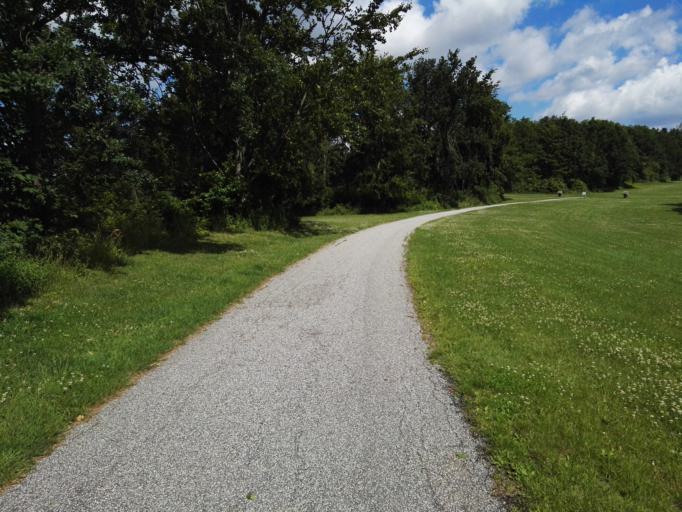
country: DK
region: Capital Region
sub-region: Ballerup Kommune
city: Ballerup
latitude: 55.7335
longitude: 12.3780
